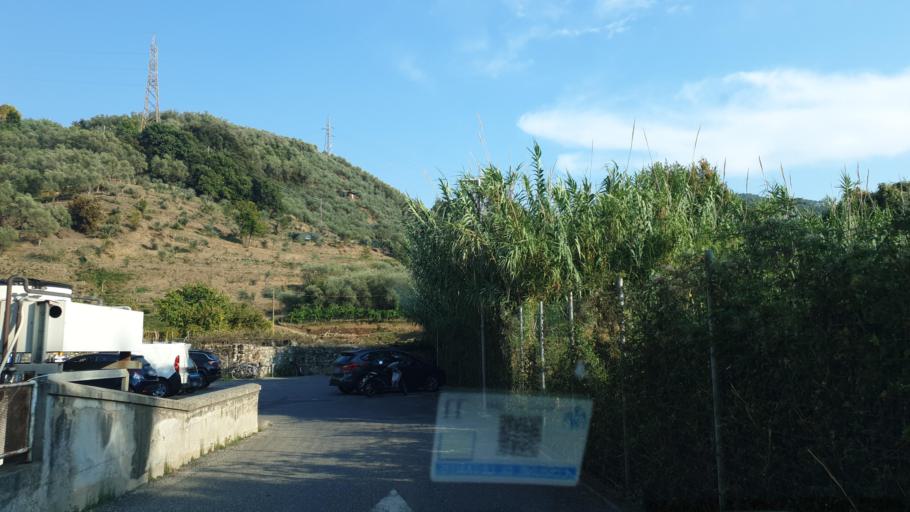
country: IT
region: Liguria
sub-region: Provincia di La Spezia
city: Levanto
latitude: 44.1779
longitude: 9.6225
